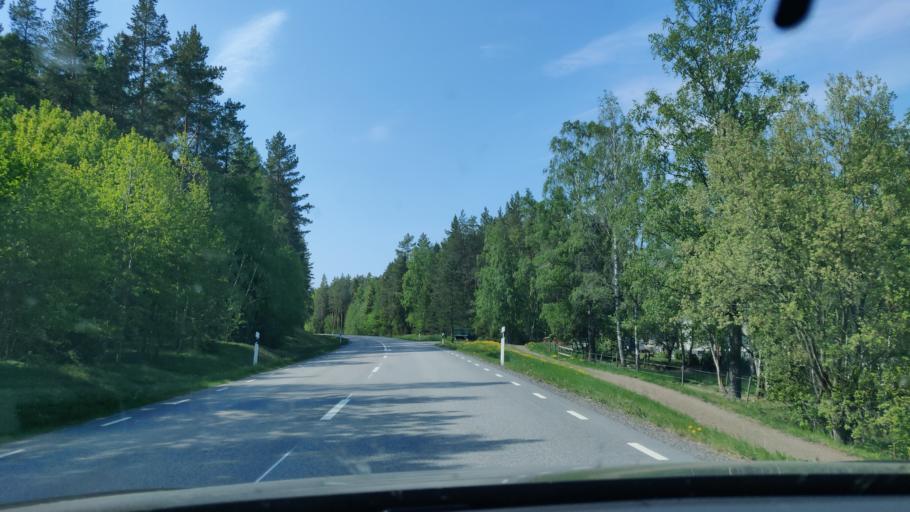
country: SE
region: Uppsala
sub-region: Heby Kommun
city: OEstervala
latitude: 60.1418
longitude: 17.2128
